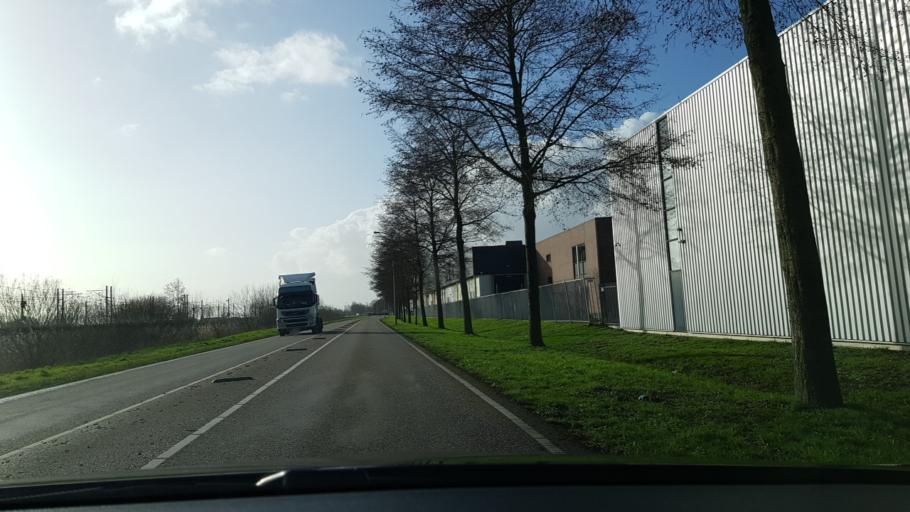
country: NL
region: South Holland
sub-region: Gemeente Kaag en Braassem
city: Leimuiden
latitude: 52.2657
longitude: 4.6540
